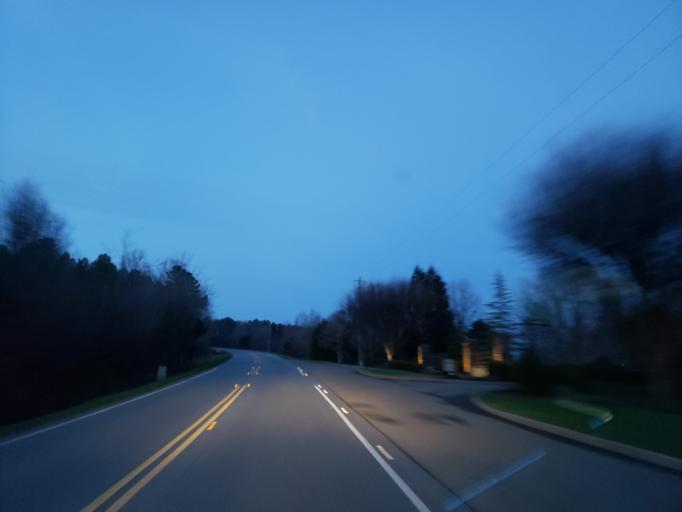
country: US
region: Georgia
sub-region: Cherokee County
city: Ball Ground
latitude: 34.3032
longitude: -84.2718
